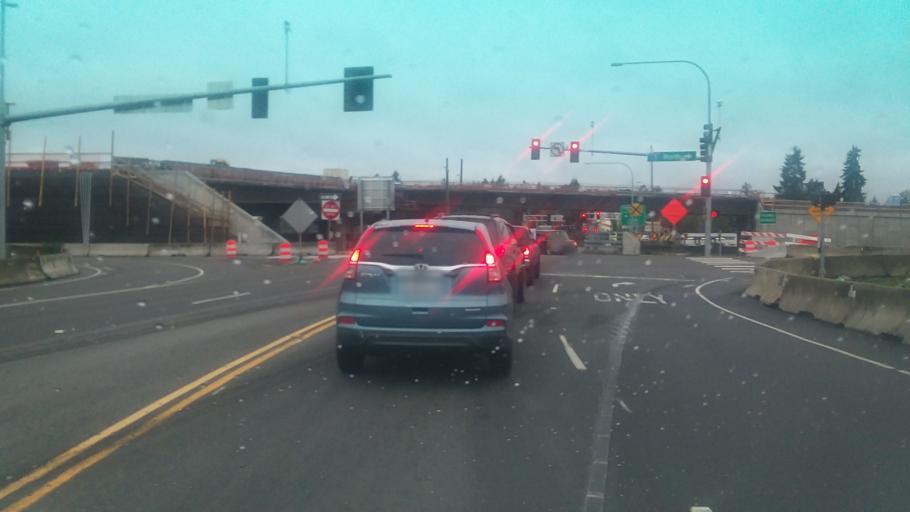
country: US
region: Washington
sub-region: Pierce County
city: Fort Lewis
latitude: 47.1180
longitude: -122.5562
